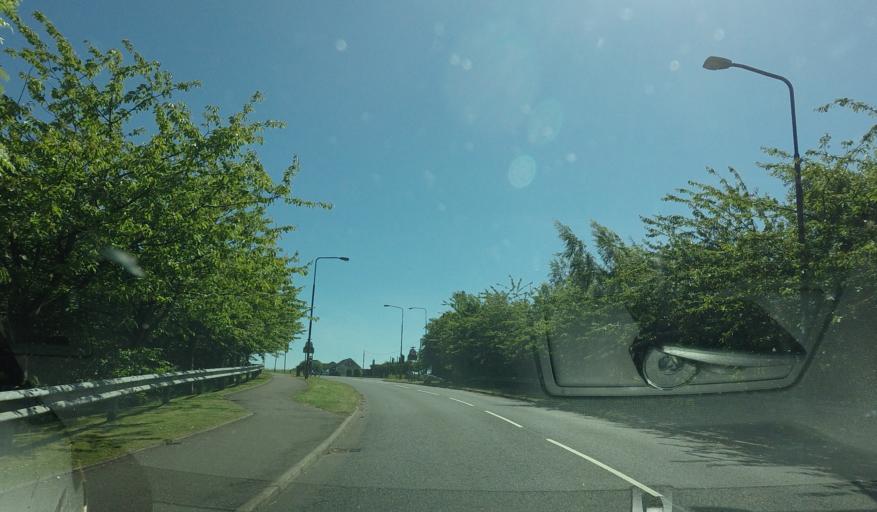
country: GB
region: Scotland
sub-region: West Lothian
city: Broxburn
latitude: 55.9293
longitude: -3.4838
